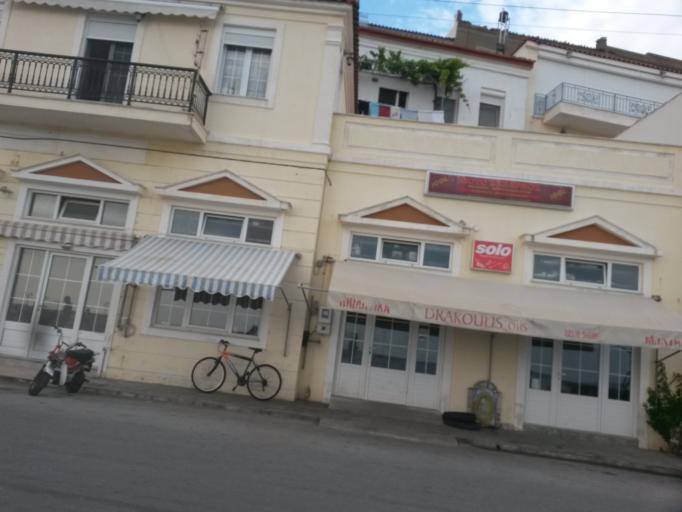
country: GR
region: North Aegean
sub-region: Nomos Lesvou
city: Plomarion
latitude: 38.9740
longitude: 26.3723
